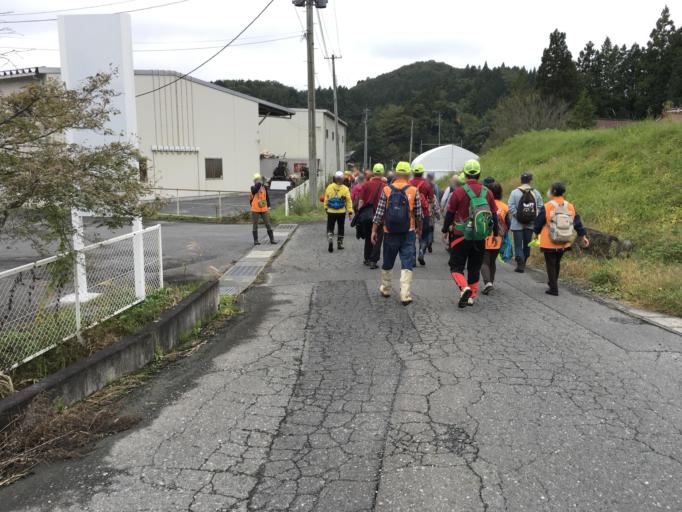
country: JP
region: Iwate
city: Ichinoseki
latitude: 38.8903
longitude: 141.1217
